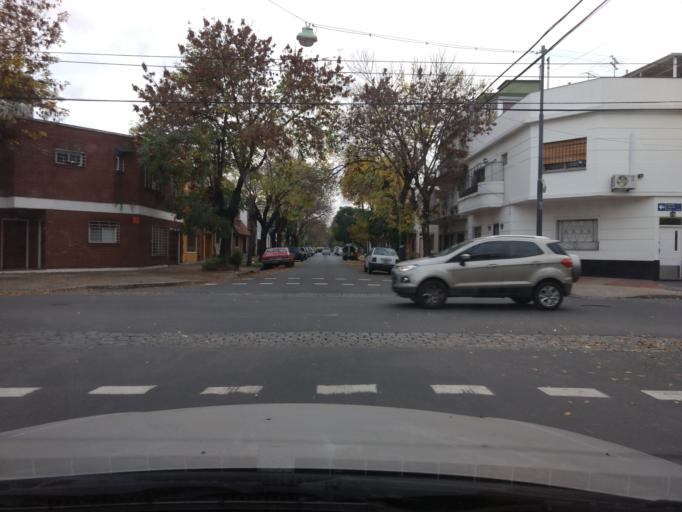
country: AR
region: Buenos Aires F.D.
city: Villa Santa Rita
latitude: -34.6110
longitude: -58.5132
